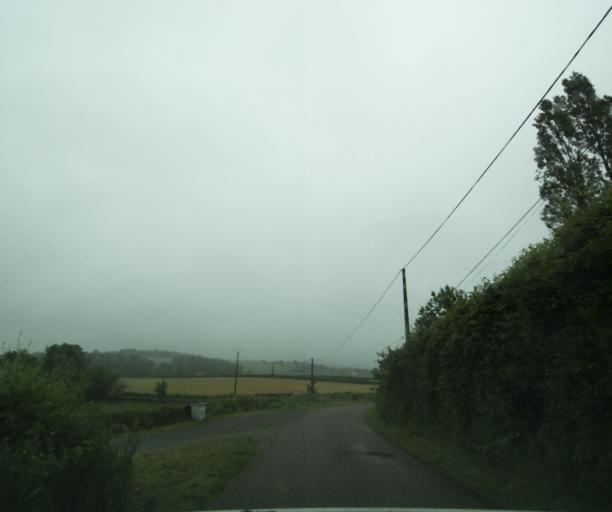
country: FR
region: Bourgogne
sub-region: Departement de Saone-et-Loire
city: Charolles
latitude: 46.4191
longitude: 4.3779
